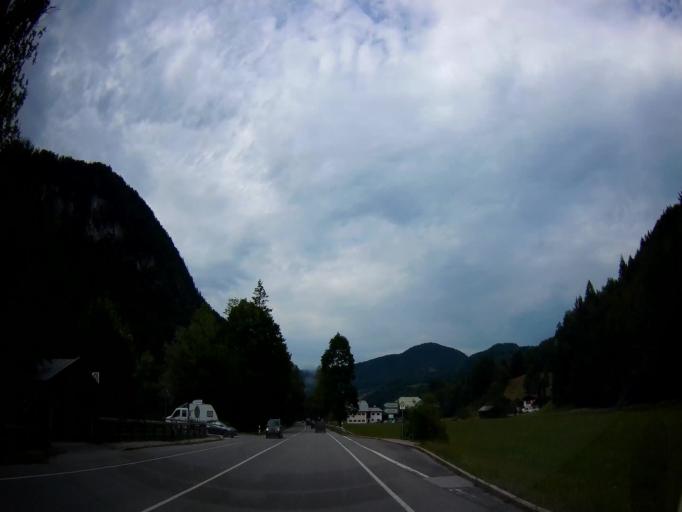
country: DE
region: Bavaria
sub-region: Upper Bavaria
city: Marktschellenberg
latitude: 47.6721
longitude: 13.0364
